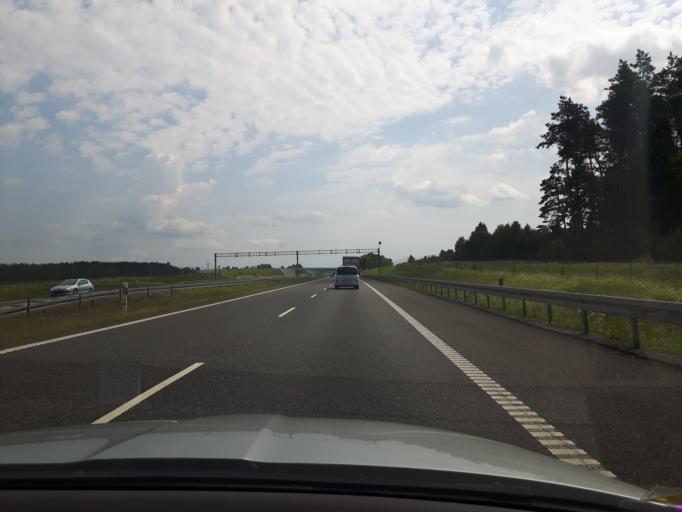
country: PL
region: Warmian-Masurian Voivodeship
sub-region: Powiat olsztynski
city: Olsztynek
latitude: 53.5190
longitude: 20.2901
